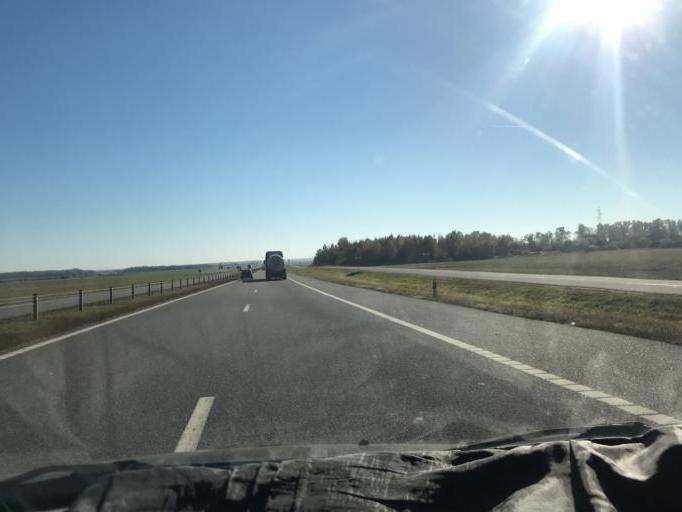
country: BY
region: Mogilev
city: Yalizava
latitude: 53.2454
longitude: 28.9407
